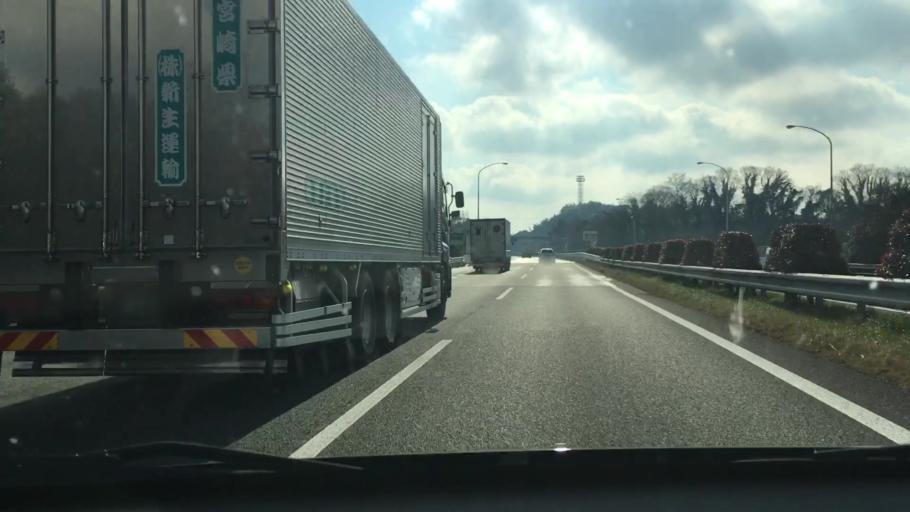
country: JP
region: Kumamoto
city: Kumamoto
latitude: 32.7320
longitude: 130.7759
